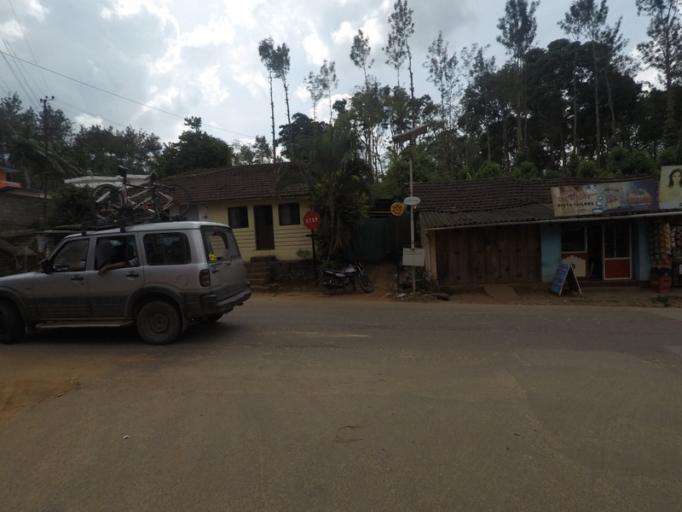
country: IN
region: Karnataka
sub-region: Kodagu
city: Virarajendrapet
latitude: 12.2949
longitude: 75.8745
